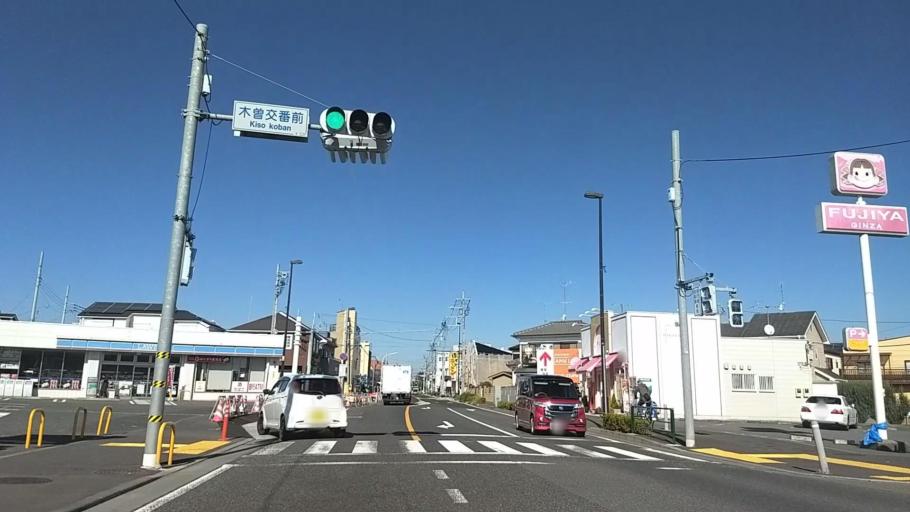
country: JP
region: Tokyo
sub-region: Machida-shi
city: Machida
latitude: 35.5636
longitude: 139.4263
